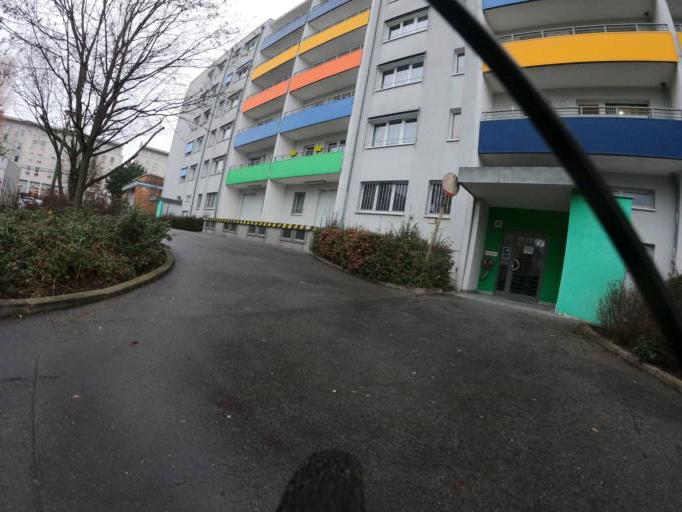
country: DE
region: Berlin
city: Marzahn
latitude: 52.5549
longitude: 13.5602
